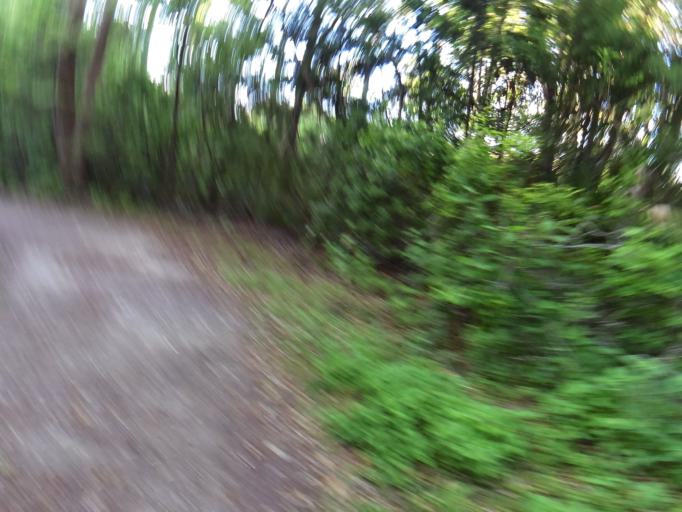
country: US
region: Florida
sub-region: Duval County
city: Atlantic Beach
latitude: 30.3835
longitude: -81.4951
